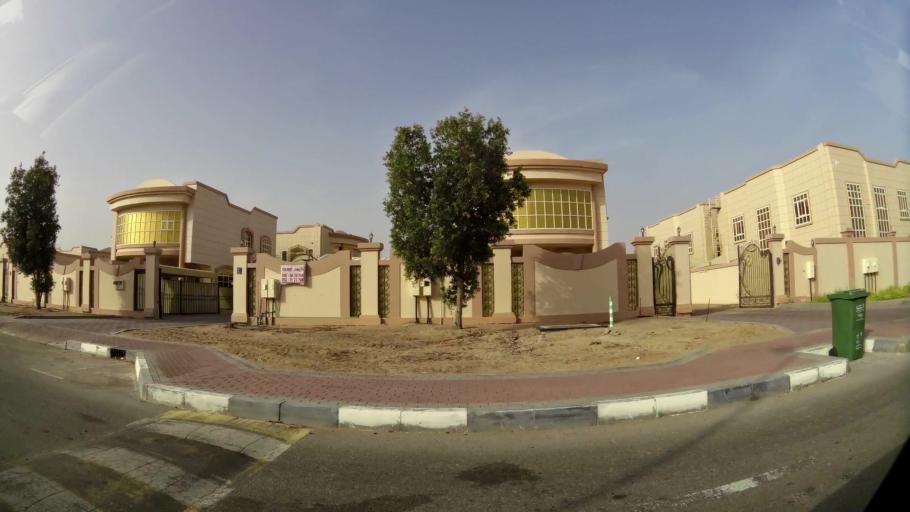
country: AE
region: Abu Dhabi
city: Al Ain
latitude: 24.1259
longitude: 55.7030
